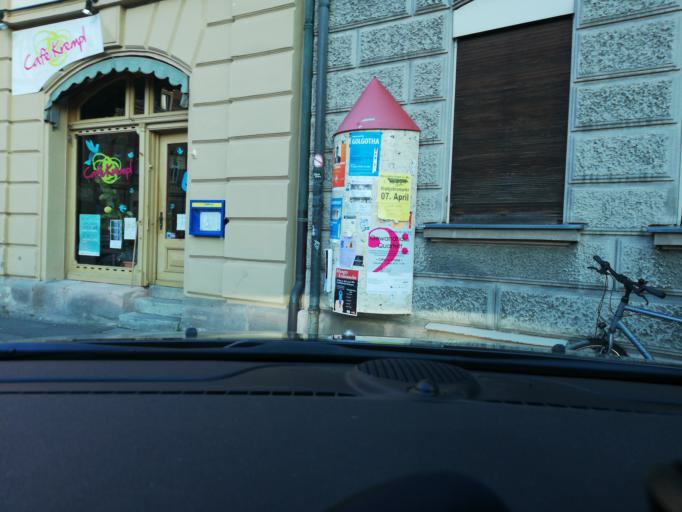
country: DE
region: Bavaria
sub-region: Regierungsbezirk Mittelfranken
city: Erlangen
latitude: 49.5980
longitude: 11.0156
